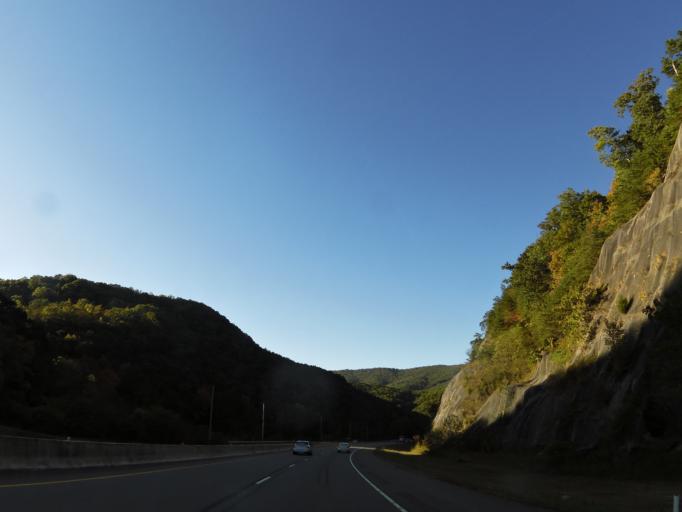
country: US
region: Tennessee
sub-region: Grainger County
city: Bean Station
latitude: 36.3469
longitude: -83.3358
